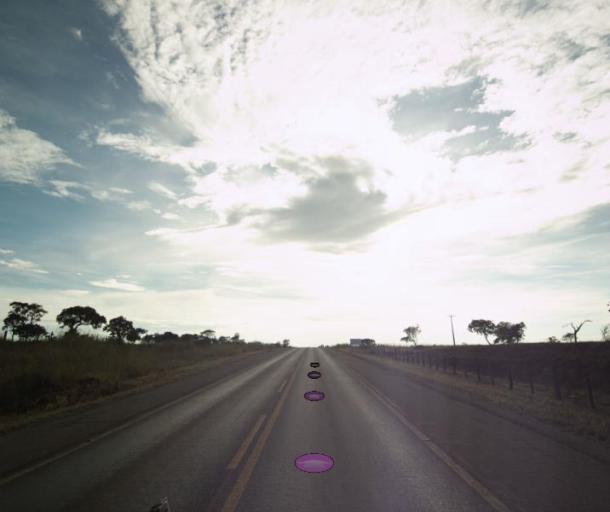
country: BR
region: Goias
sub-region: Pirenopolis
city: Pirenopolis
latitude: -15.7563
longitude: -48.6844
